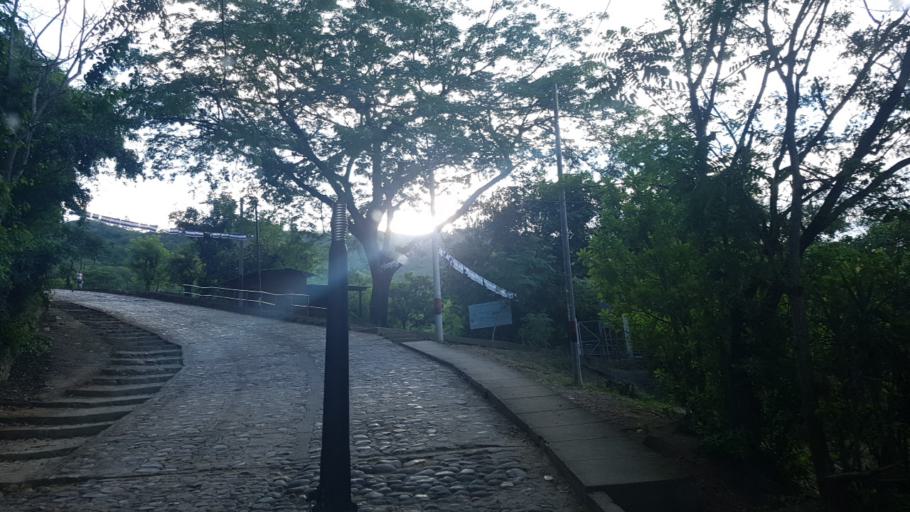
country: NI
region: Nueva Segovia
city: Ocotal
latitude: 13.6534
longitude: -86.6132
